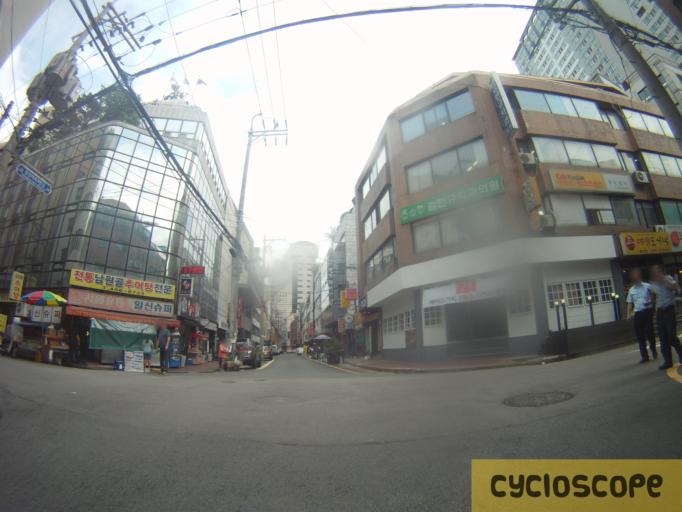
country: KR
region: Busan
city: Busan
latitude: 35.1055
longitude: 129.0375
